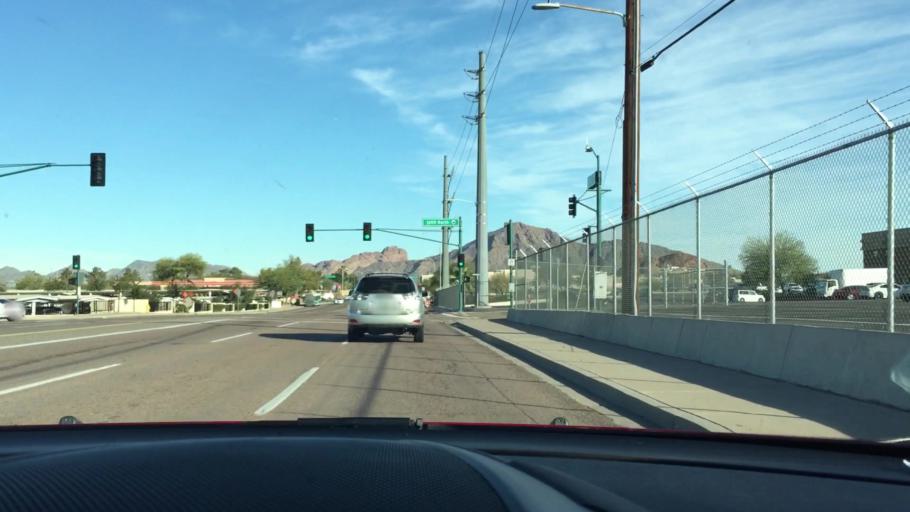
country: US
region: Arizona
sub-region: Maricopa County
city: Tempe Junction
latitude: 33.4633
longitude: -111.9684
